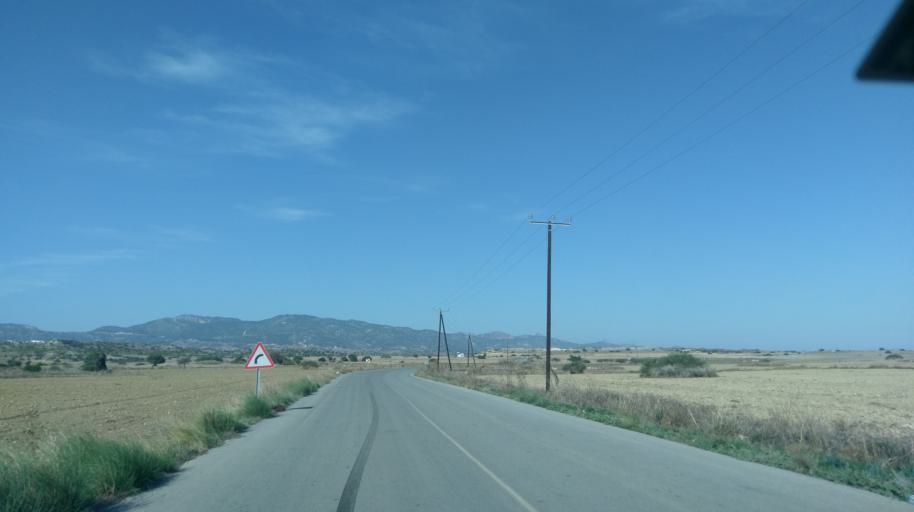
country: CY
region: Ammochostos
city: Trikomo
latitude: 35.3039
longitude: 33.8908
